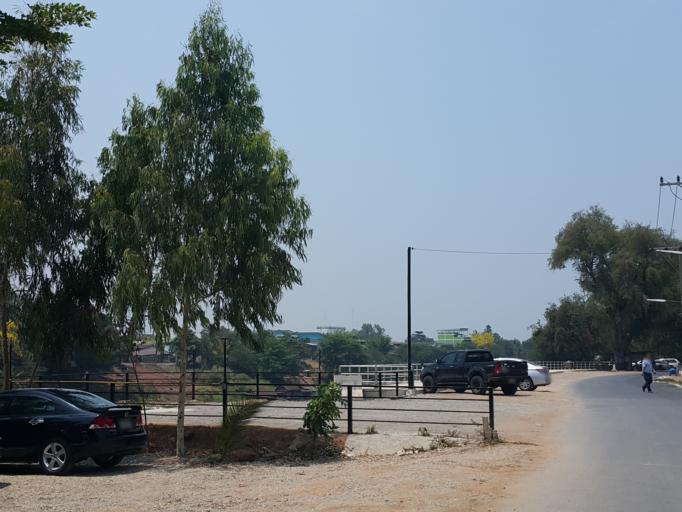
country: TH
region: Phitsanulok
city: Phitsanulok
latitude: 16.8108
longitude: 100.2559
